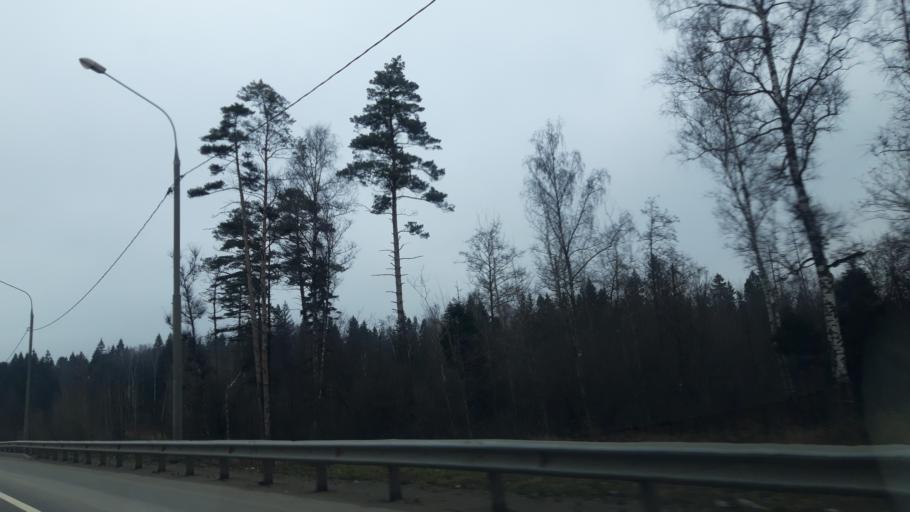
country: RU
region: Moskovskaya
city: Lozhki
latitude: 56.0827
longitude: 37.1204
